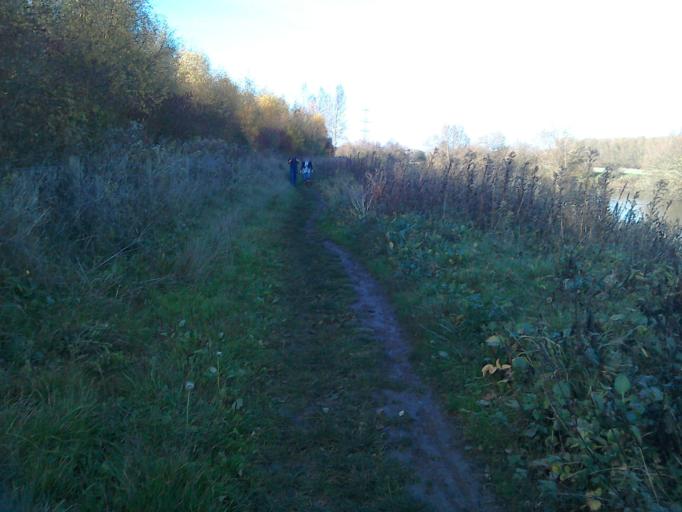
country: GB
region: England
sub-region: Oxfordshire
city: Radley
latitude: 51.7006
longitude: -1.2317
